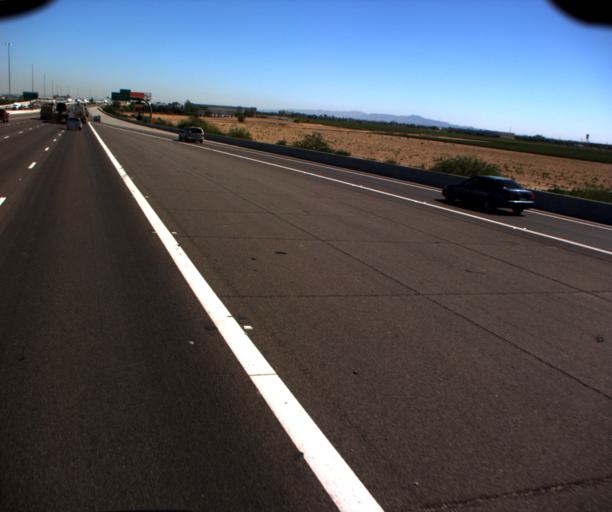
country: US
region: Arizona
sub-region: Maricopa County
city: Goodyear
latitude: 33.4611
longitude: -112.3890
